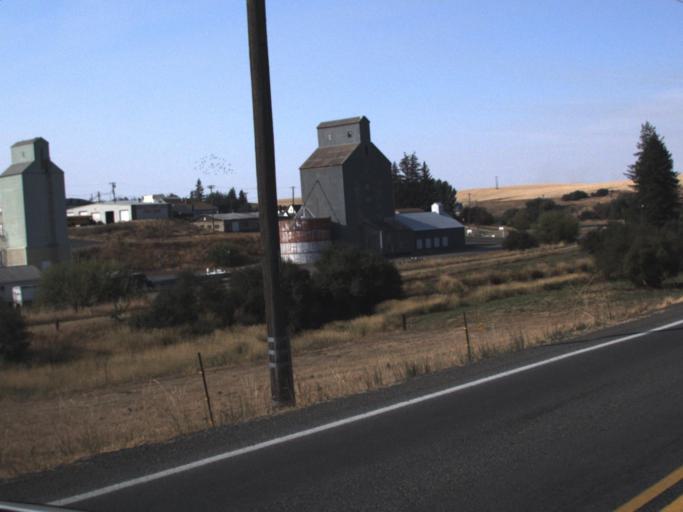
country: US
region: Idaho
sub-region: Benewah County
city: Plummer
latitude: 47.2268
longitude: -117.0695
